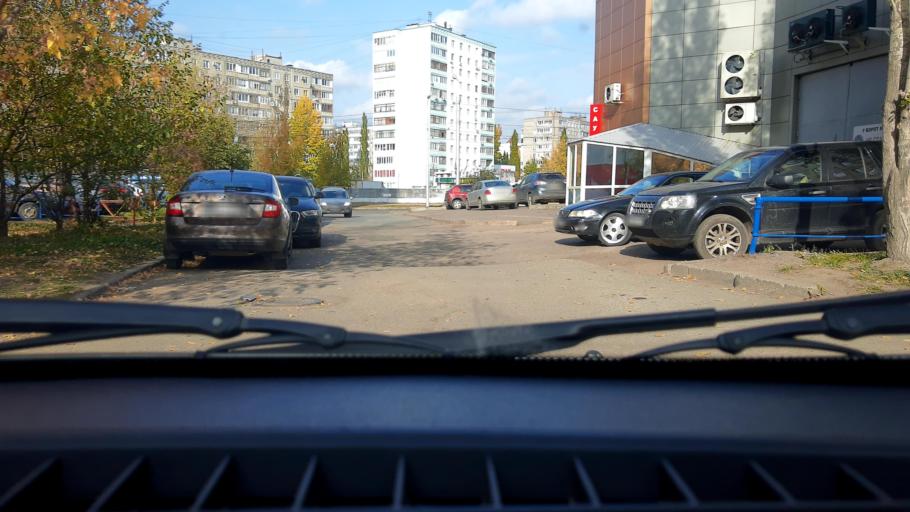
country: RU
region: Bashkortostan
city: Ufa
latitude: 54.7637
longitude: 56.0623
